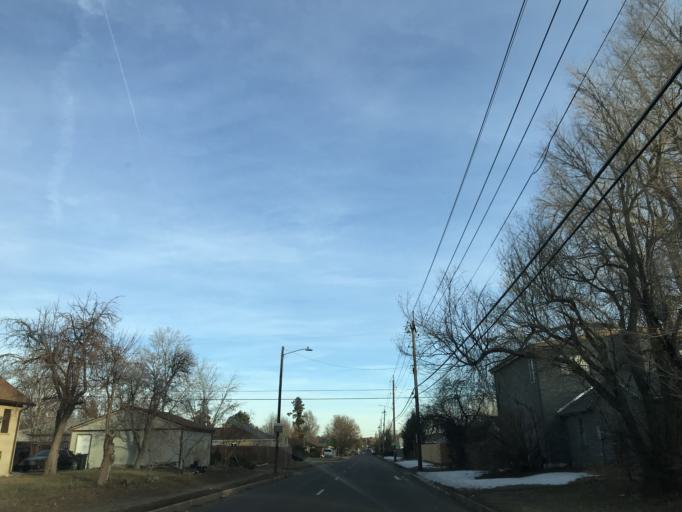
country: US
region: Colorado
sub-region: Arapahoe County
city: Glendale
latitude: 39.7387
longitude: -104.8906
